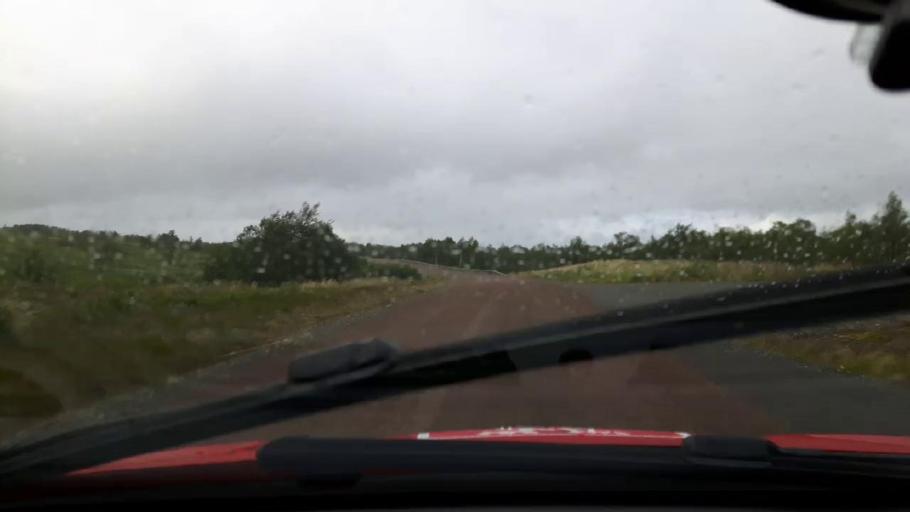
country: NO
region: Nord-Trondelag
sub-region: Meraker
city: Meraker
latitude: 63.2088
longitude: 12.4035
